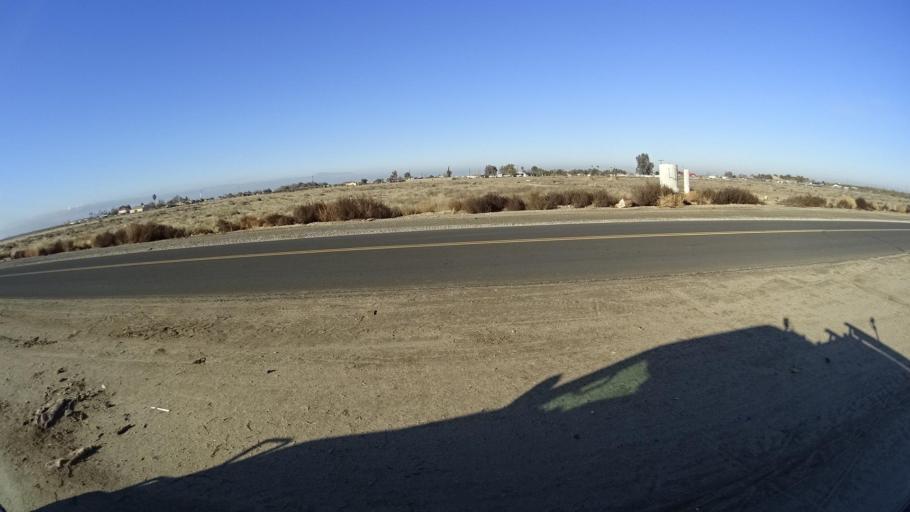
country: US
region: California
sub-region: Kern County
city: Delano
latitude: 35.7719
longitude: -119.2757
